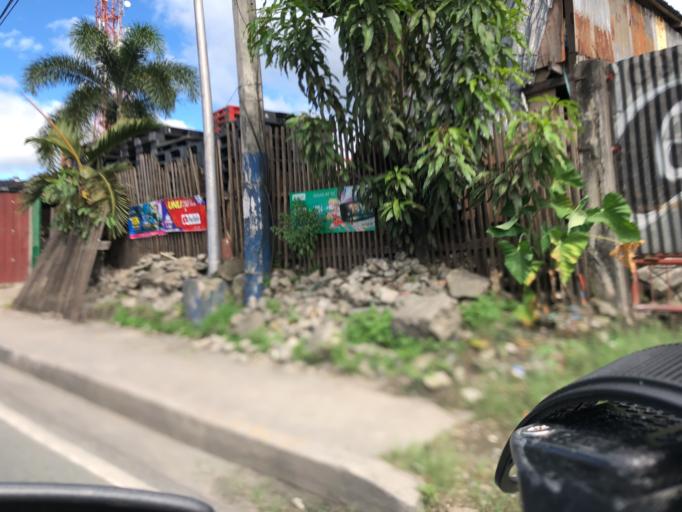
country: PH
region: Calabarzon
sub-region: Province of Rizal
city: San Mateo
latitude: 14.7261
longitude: 121.0612
